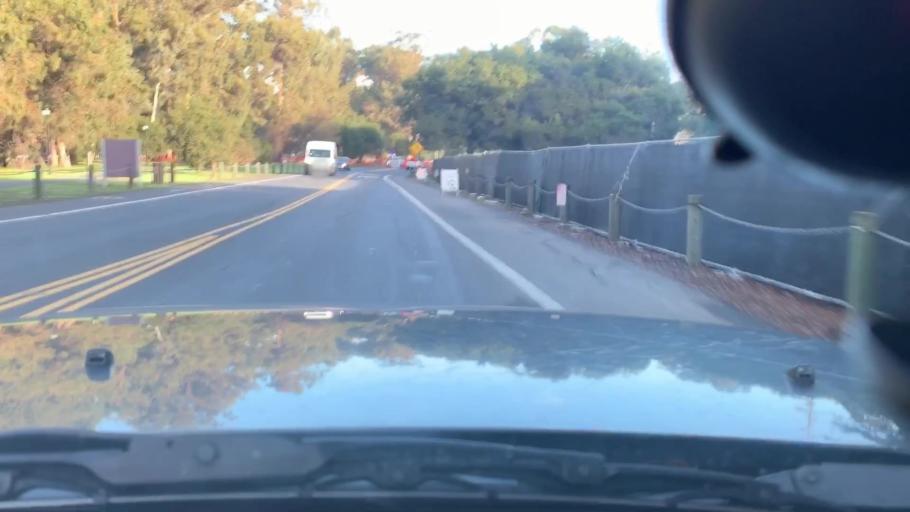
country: US
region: California
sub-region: Santa Clara County
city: Stanford
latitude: 37.4345
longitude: -122.1632
